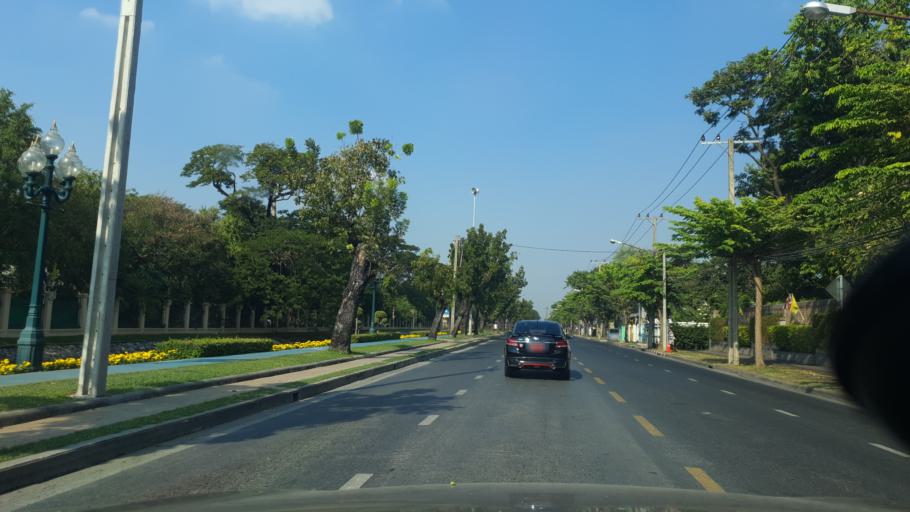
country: TH
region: Bangkok
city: Dusit
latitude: 13.7710
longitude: 100.5247
